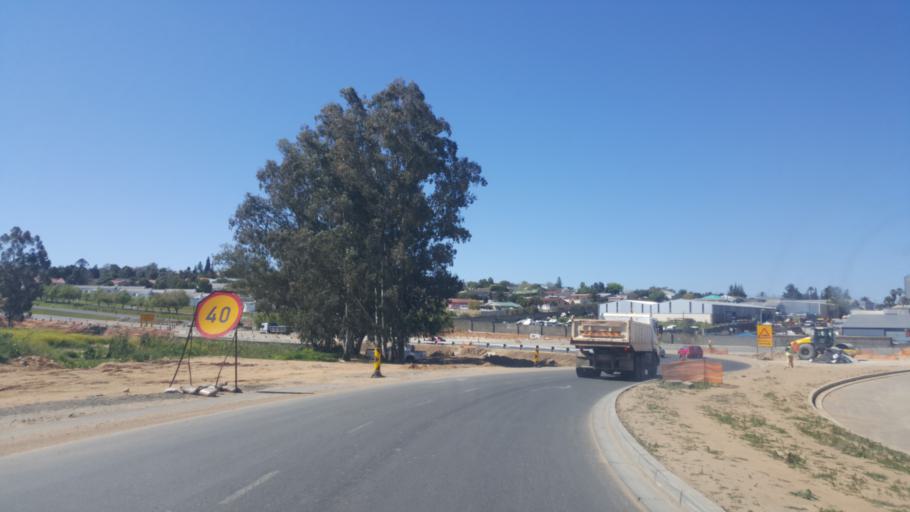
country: ZA
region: Western Cape
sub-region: West Coast District Municipality
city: Malmesbury
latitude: -33.4644
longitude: 18.7167
